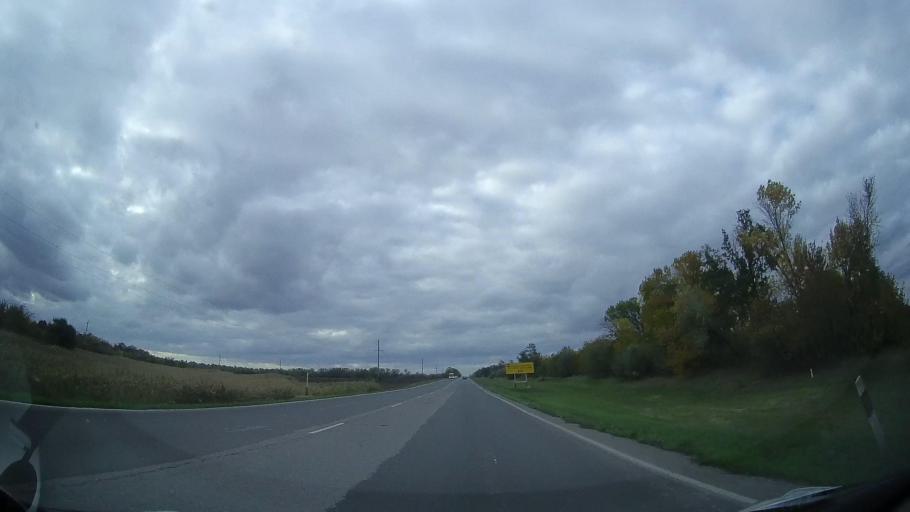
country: RU
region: Rostov
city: Mechetinskaya
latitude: 46.7936
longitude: 40.3860
